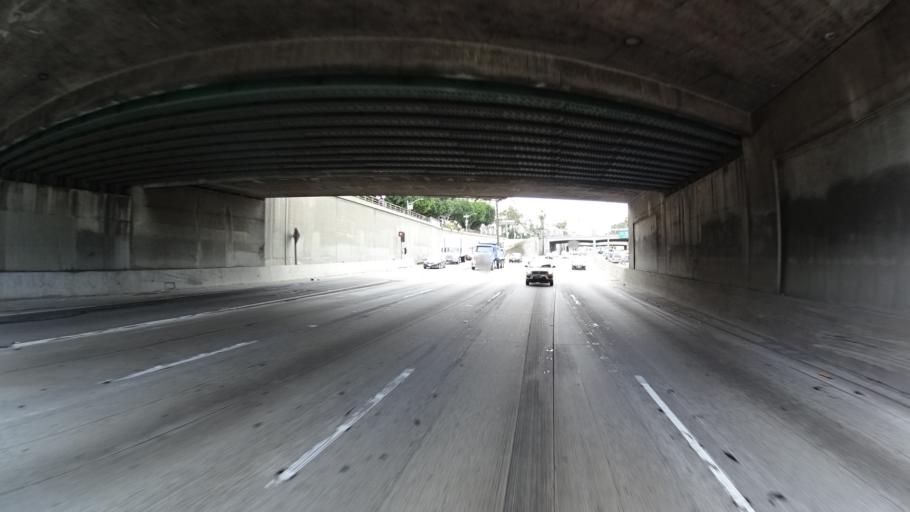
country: US
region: California
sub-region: Los Angeles County
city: Los Angeles
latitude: 34.0542
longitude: -118.2381
